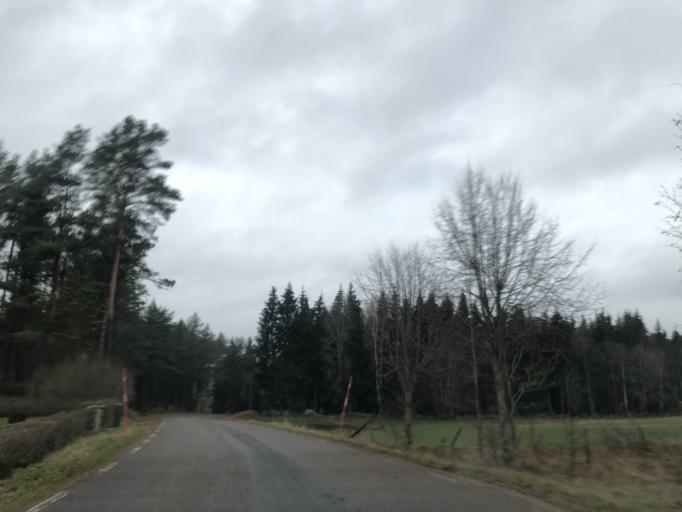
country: SE
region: Vaestra Goetaland
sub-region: Ulricehamns Kommun
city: Ulricehamn
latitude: 57.8720
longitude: 13.5459
